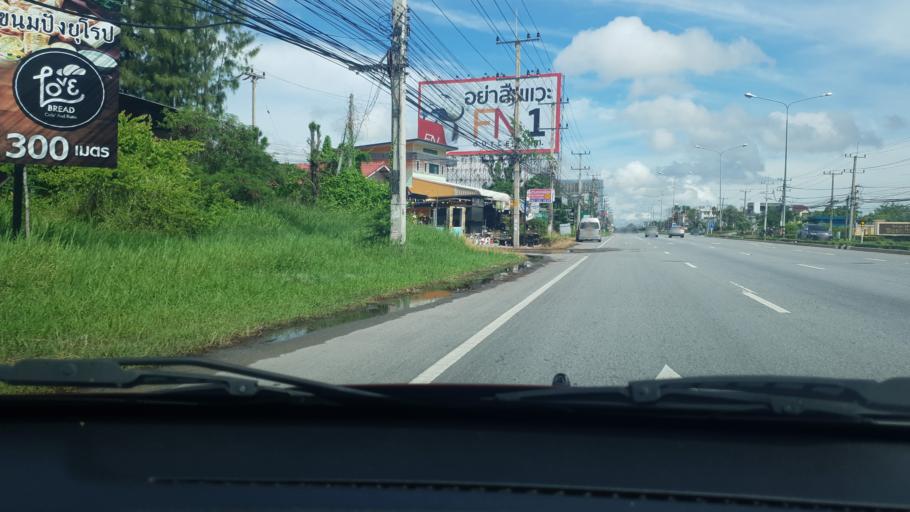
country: TH
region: Prachuap Khiri Khan
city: Hua Hin
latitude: 12.6577
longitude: 99.9520
